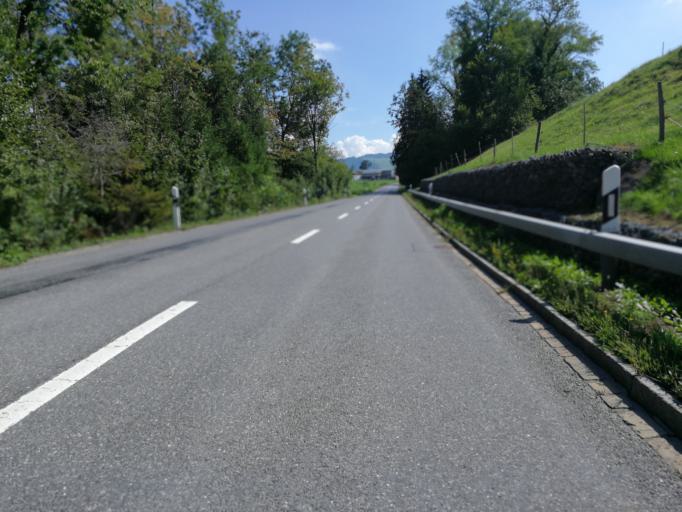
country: CH
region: Zurich
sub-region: Bezirk Horgen
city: Au
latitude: 47.2222
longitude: 8.6307
